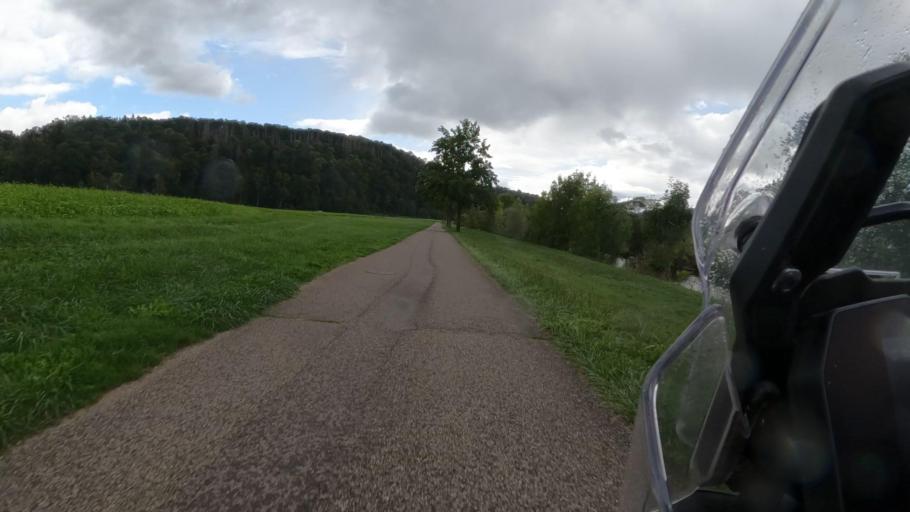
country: DE
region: Baden-Wuerttemberg
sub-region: Freiburg Region
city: Eggingen
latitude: 47.6832
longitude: 8.3842
